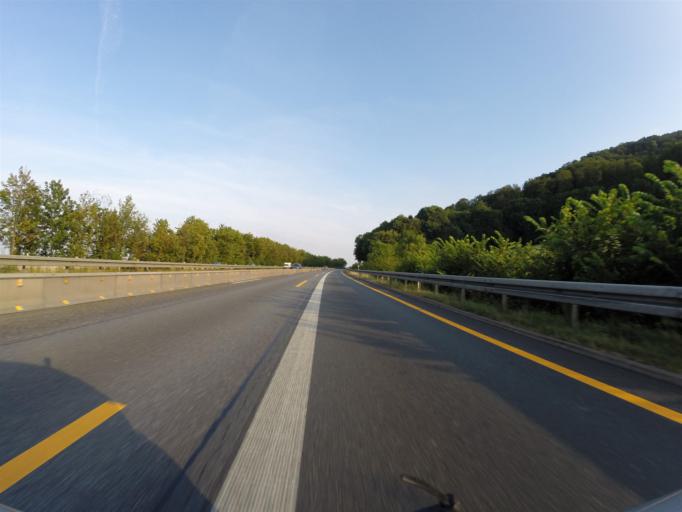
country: DE
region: Hesse
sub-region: Regierungsbezirk Kassel
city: Zierenberg
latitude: 51.3720
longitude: 9.2783
